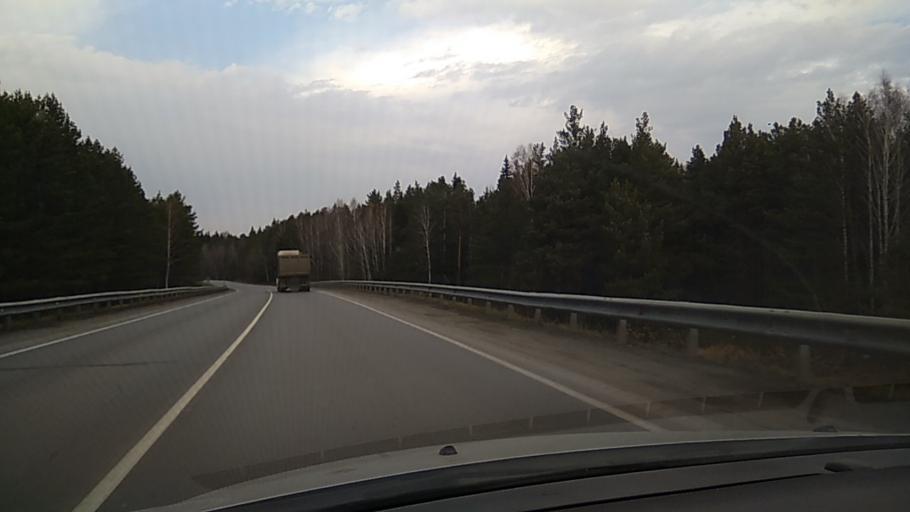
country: RU
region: Sverdlovsk
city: Tugulym
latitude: 57.0684
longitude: 64.6461
